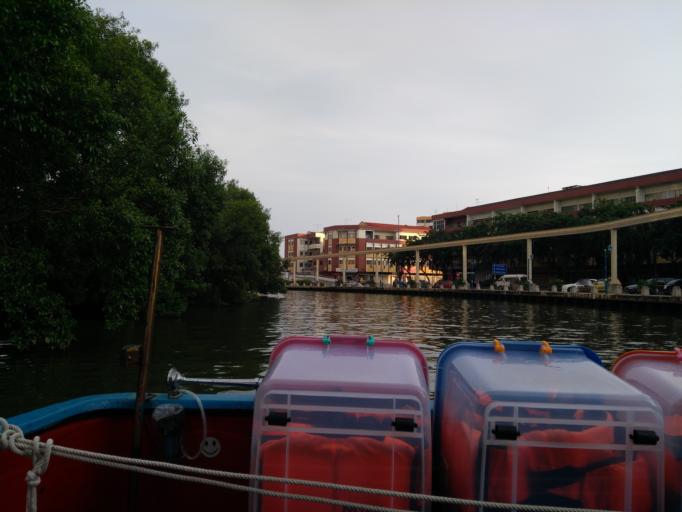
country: MY
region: Melaka
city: Malacca
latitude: 2.2029
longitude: 102.2492
